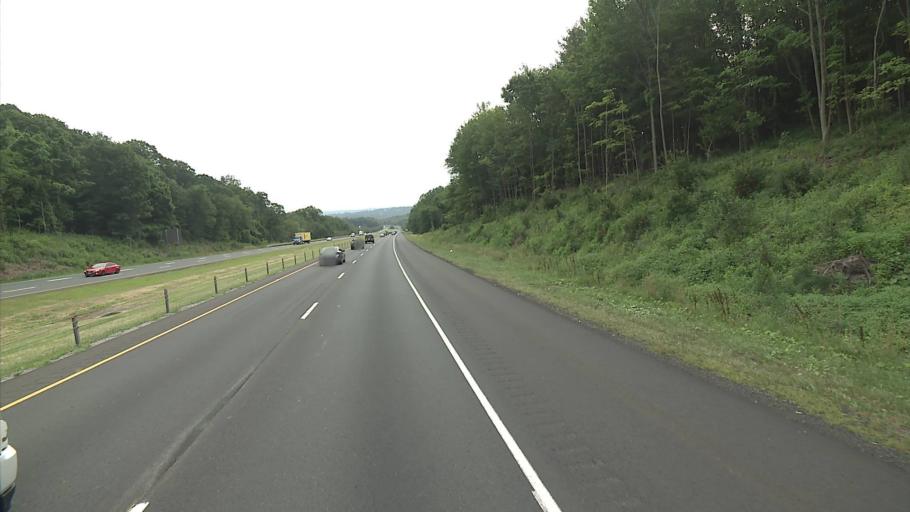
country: US
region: Connecticut
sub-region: New Haven County
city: Middlebury
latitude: 41.5152
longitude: -73.1171
